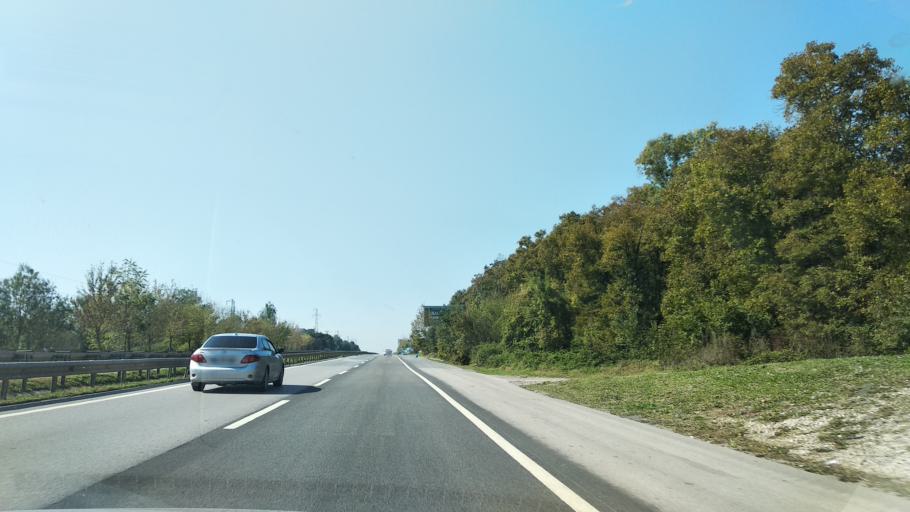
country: TR
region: Kocaeli
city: Derbent
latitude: 40.7316
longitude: 30.1672
